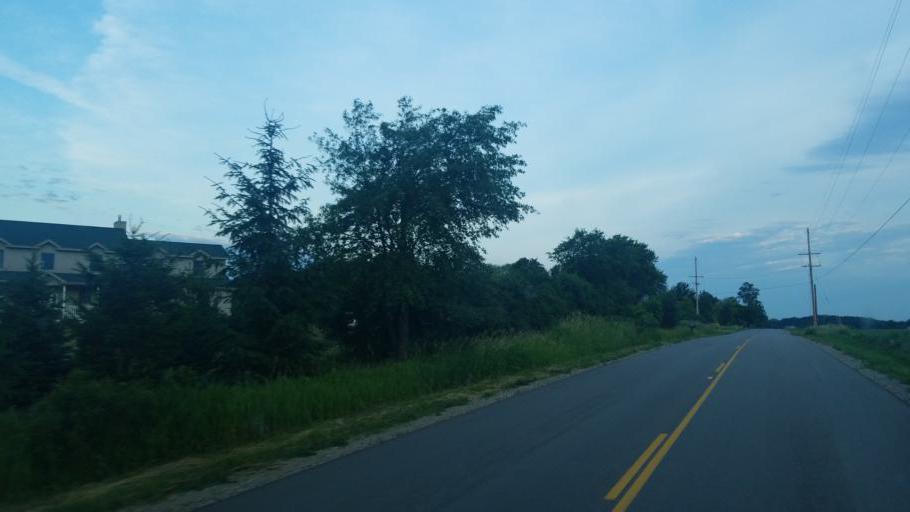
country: US
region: Michigan
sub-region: Eaton County
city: Charlotte
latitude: 42.5970
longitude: -84.8393
